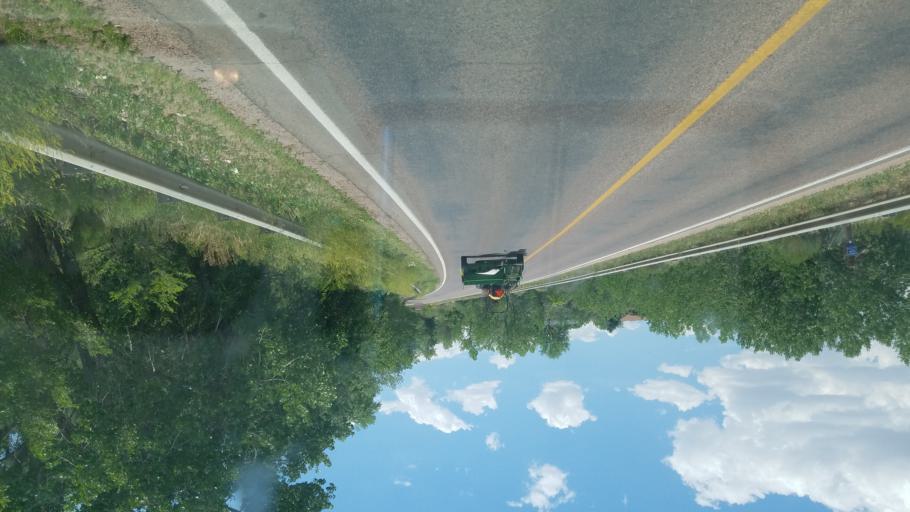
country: US
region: Colorado
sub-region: Fremont County
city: Lincoln Park
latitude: 38.4337
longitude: -105.2000
